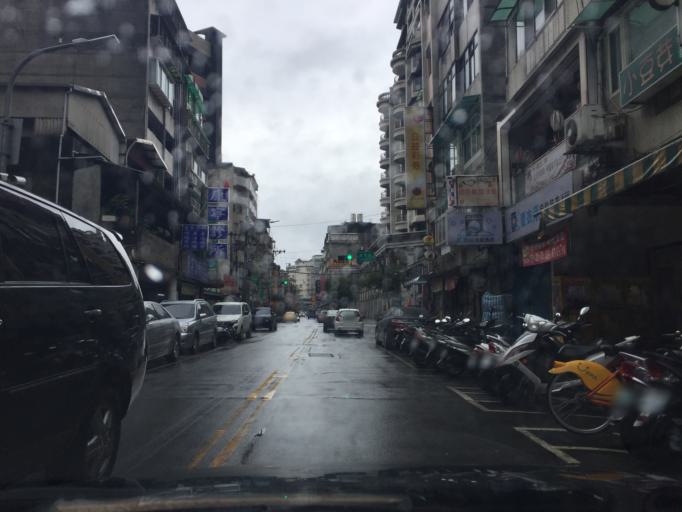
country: TW
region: Taipei
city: Taipei
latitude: 25.0792
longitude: 121.5943
